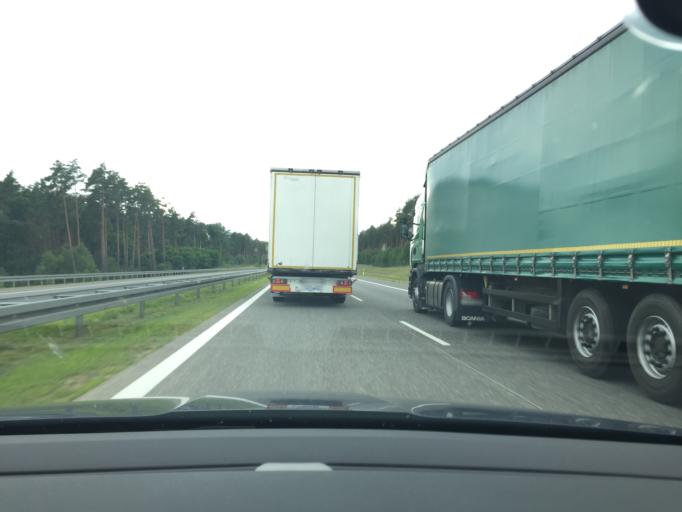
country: PL
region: Lubusz
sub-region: Powiat swiebodzinski
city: Lubrza
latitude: 52.3182
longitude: 15.4842
